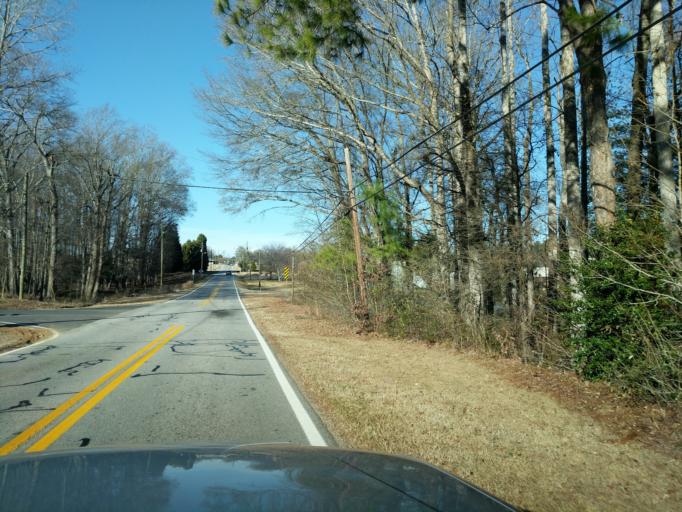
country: US
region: Georgia
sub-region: Hart County
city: Hartwell
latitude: 34.3455
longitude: -82.9193
